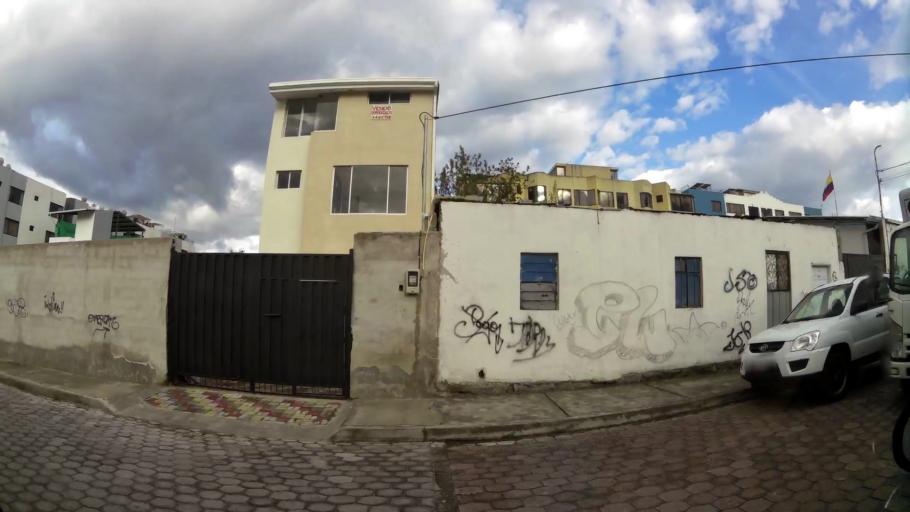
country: EC
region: Pichincha
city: Quito
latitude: -0.1309
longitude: -78.4629
